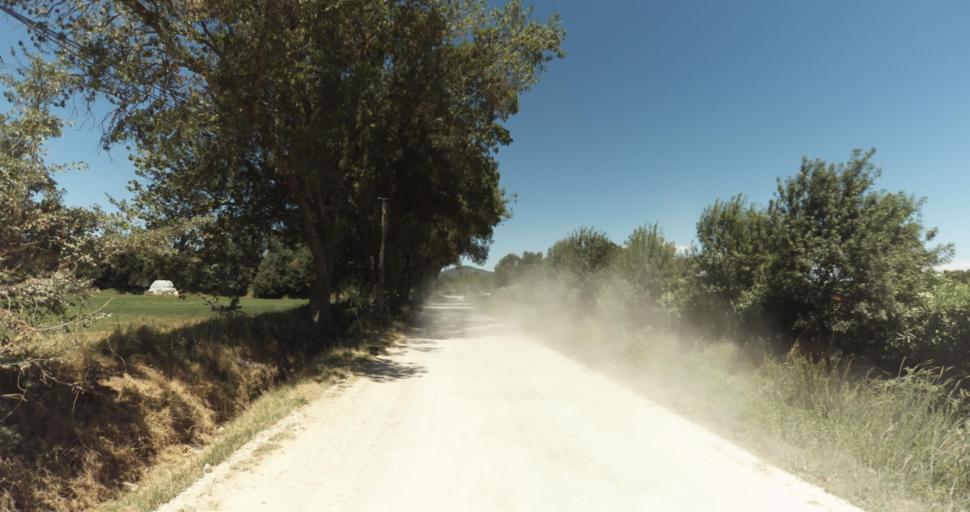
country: FR
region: Provence-Alpes-Cote d'Azur
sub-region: Departement du Var
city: Gassin
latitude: 43.2549
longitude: 6.5762
